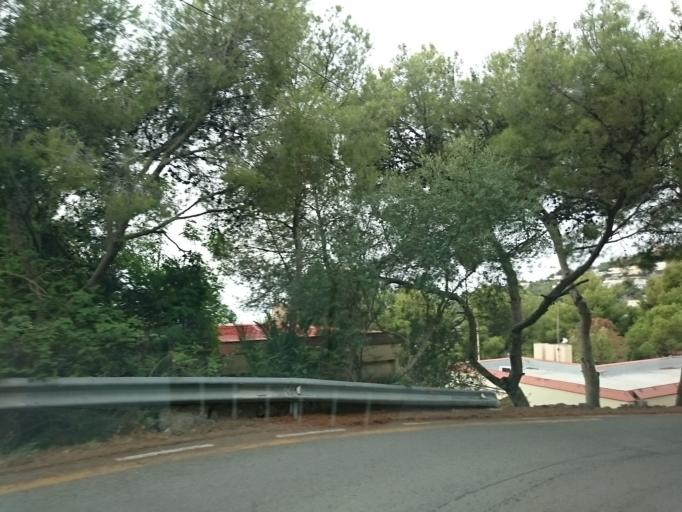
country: ES
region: Catalonia
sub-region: Provincia de Barcelona
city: Castelldefels
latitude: 41.2678
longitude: 1.9281
